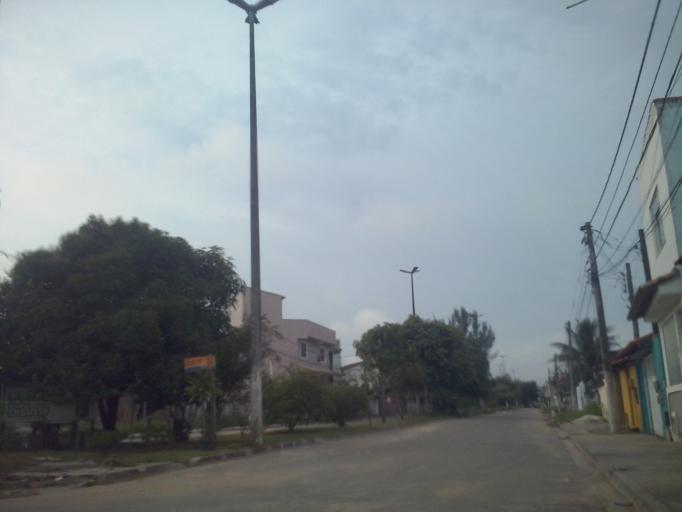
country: BR
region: Rio de Janeiro
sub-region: Rio Das Ostras
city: Rio das Ostras
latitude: -22.5273
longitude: -41.9661
